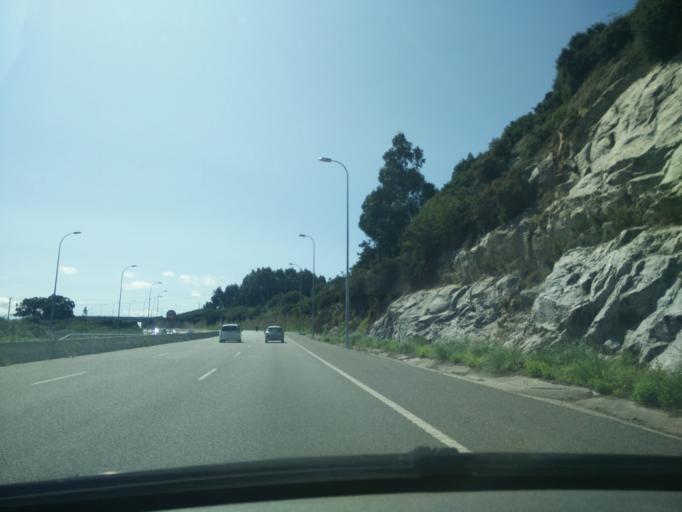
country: ES
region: Galicia
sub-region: Provincia da Coruna
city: A Coruna
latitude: 43.3641
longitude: -8.4324
